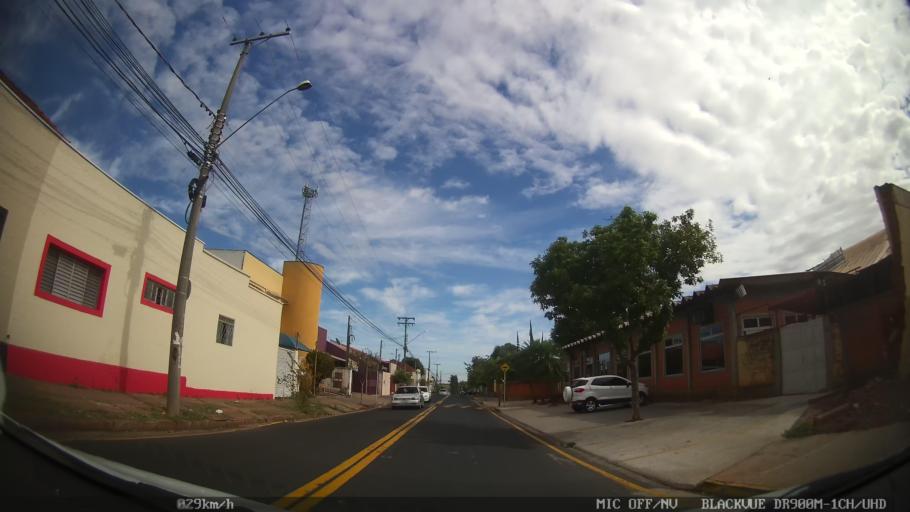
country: BR
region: Sao Paulo
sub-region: Bady Bassitt
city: Bady Bassitt
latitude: -20.8152
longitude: -49.5185
